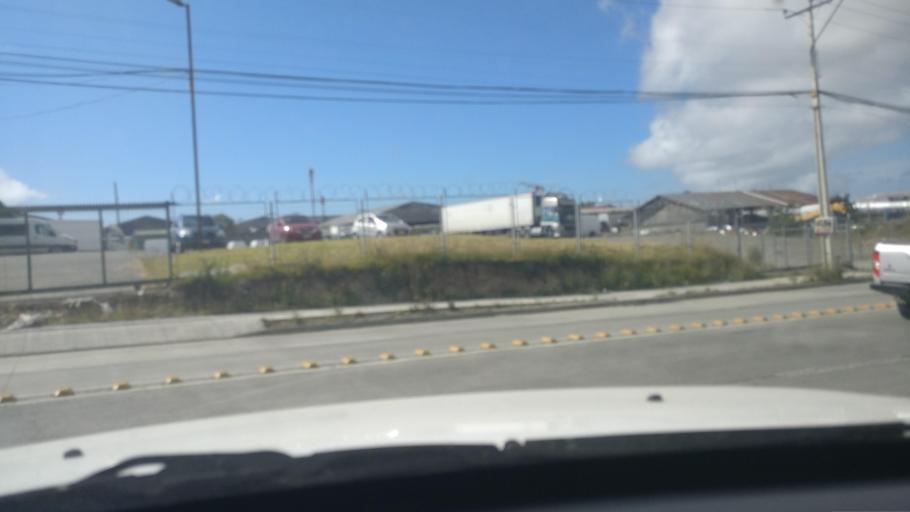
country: CL
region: Los Lagos
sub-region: Provincia de Llanquihue
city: Puerto Montt
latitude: -41.4531
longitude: -72.9635
